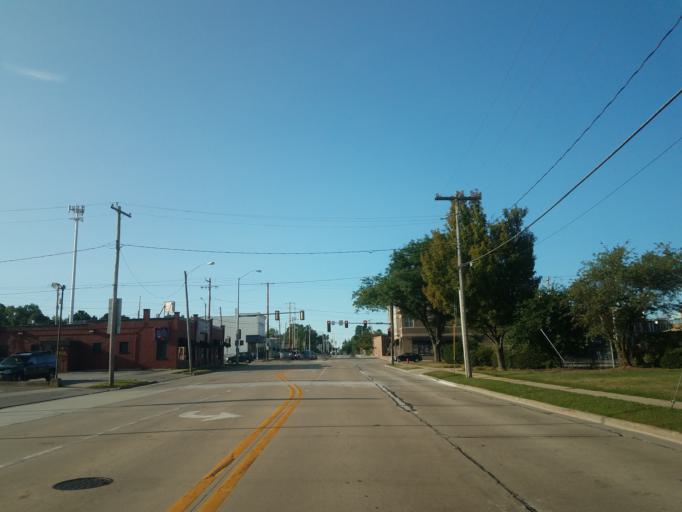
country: US
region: Illinois
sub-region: McLean County
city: Normal
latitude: 40.5112
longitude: -88.9825
